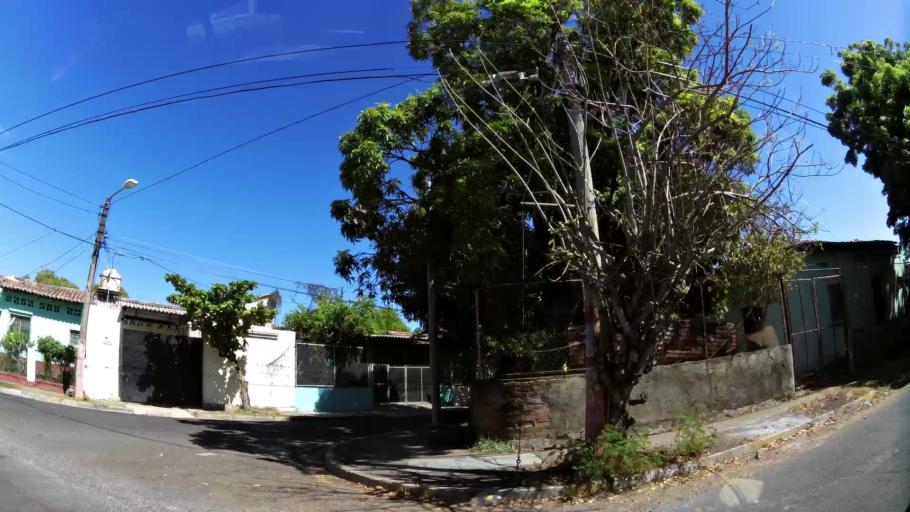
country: SV
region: San Miguel
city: San Miguel
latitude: 13.4776
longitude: -88.1694
